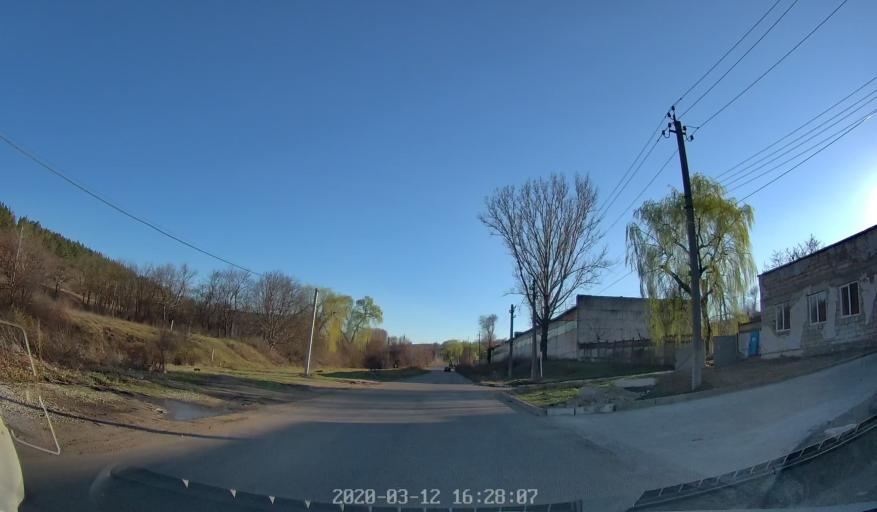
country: MD
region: Anenii Noi
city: Anenii Noi
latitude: 46.8706
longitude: 29.2260
